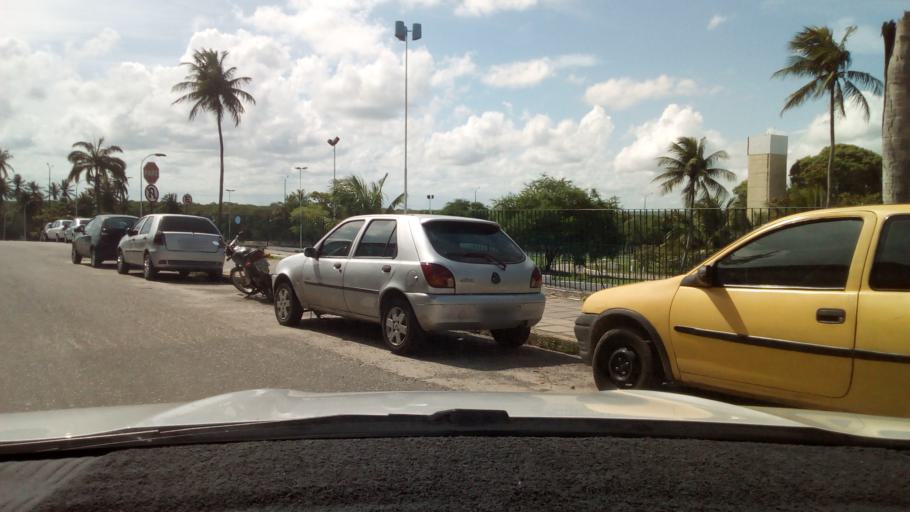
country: BR
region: Paraiba
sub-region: Joao Pessoa
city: Joao Pessoa
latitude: -7.1202
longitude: -34.8912
